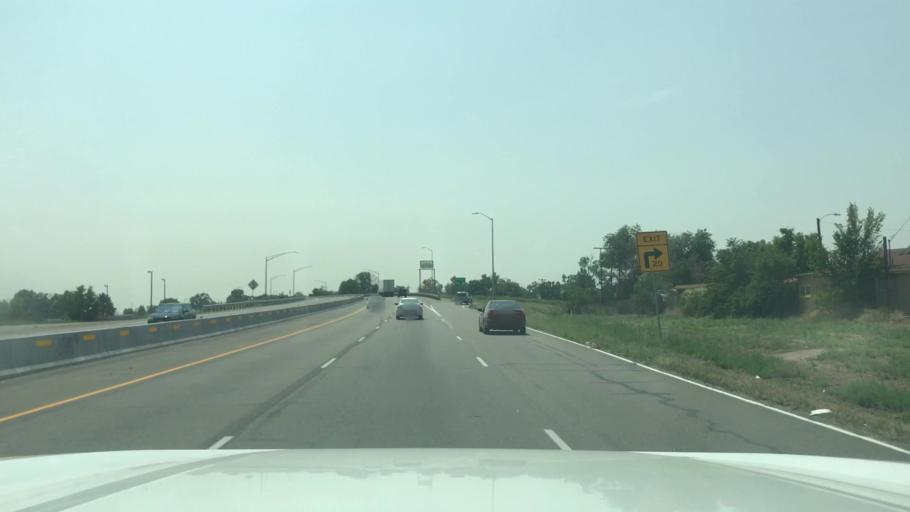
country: US
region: Colorado
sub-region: Pueblo County
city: Pueblo
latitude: 38.2345
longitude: -104.6130
